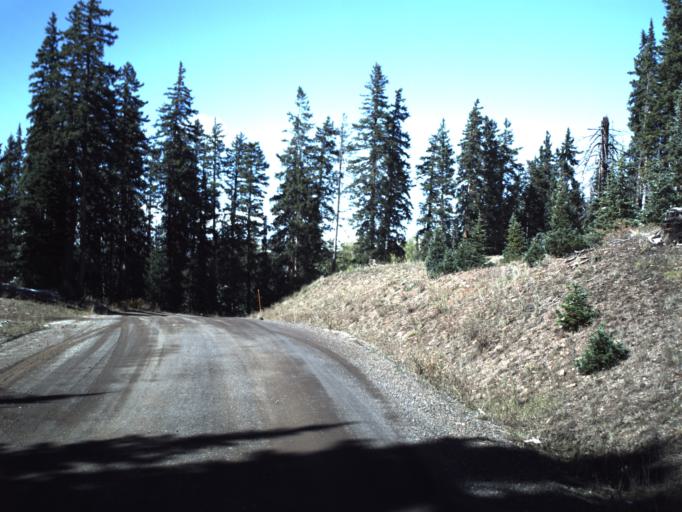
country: US
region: Utah
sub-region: Piute County
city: Junction
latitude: 38.3037
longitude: -112.3594
